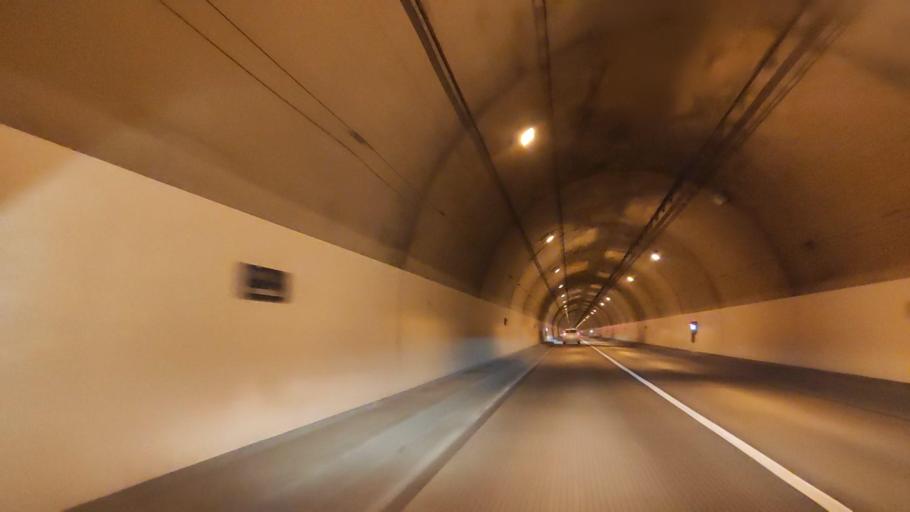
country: JP
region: Hokkaido
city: Ishikari
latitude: 43.4645
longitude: 141.4018
